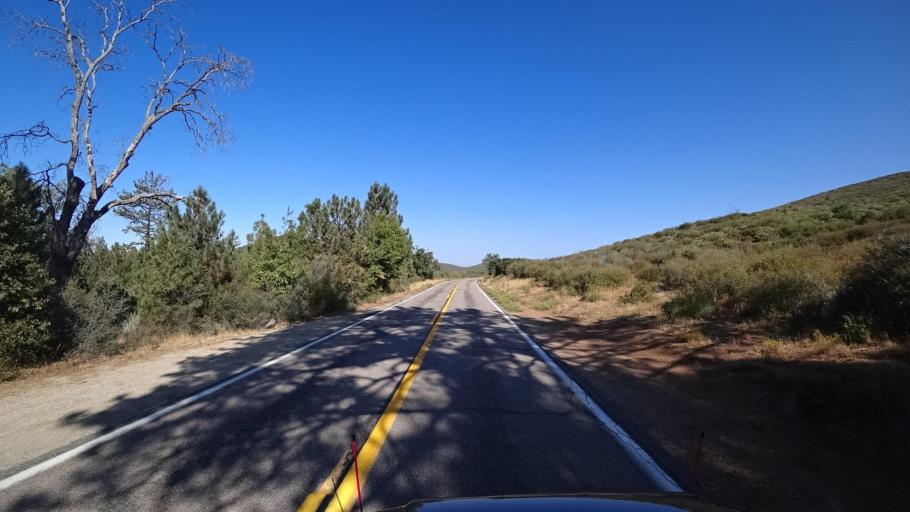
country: US
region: California
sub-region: San Diego County
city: Pine Valley
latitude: 32.9066
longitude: -116.4581
